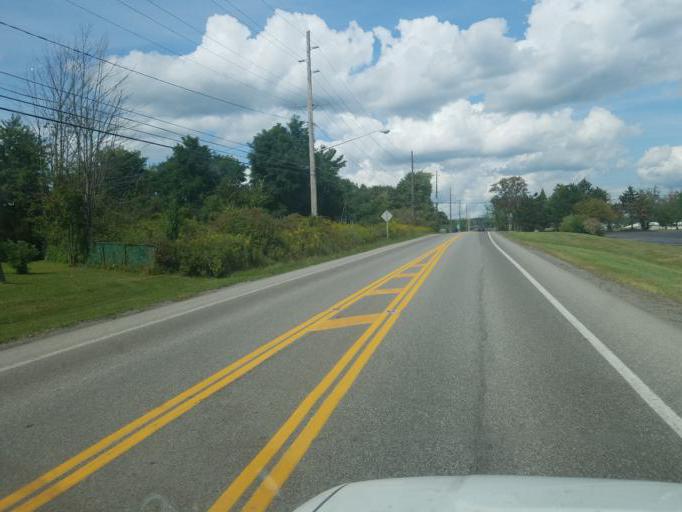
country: US
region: Ohio
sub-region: Geauga County
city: Middlefield
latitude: 41.4450
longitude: -81.0670
